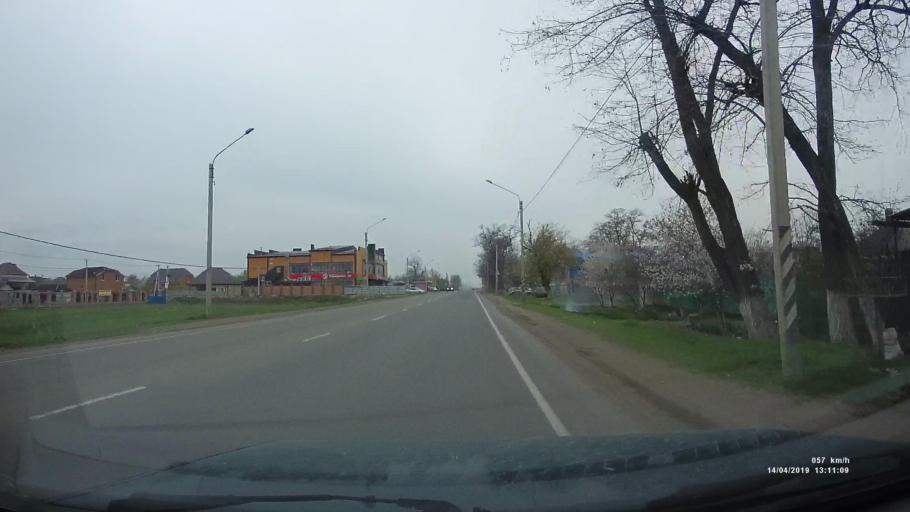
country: RU
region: Rostov
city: Kuleshovka
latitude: 47.1063
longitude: 39.6452
